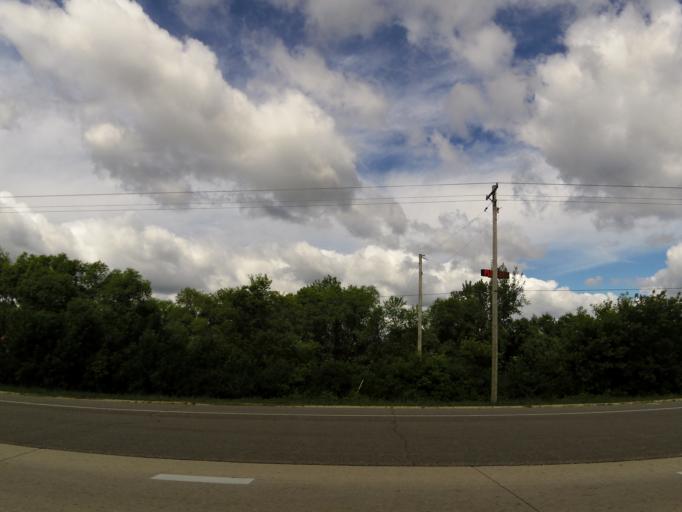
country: US
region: Minnesota
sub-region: Olmsted County
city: Stewartville
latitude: 43.8828
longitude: -92.4884
